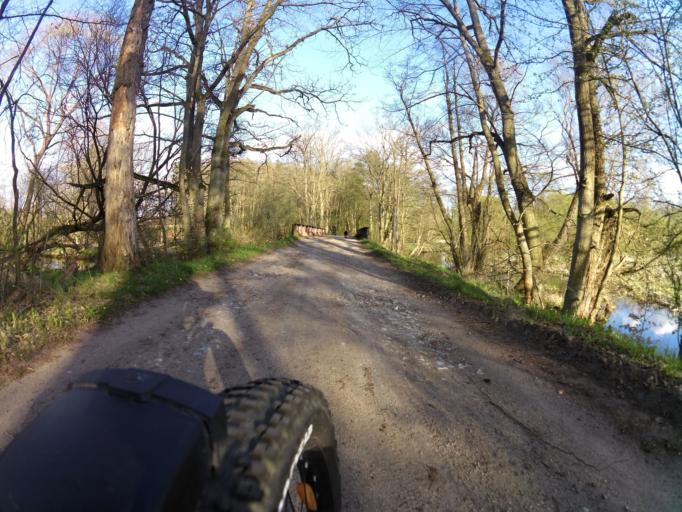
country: PL
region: West Pomeranian Voivodeship
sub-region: Powiat gryficki
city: Ploty
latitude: 53.7440
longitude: 15.2639
